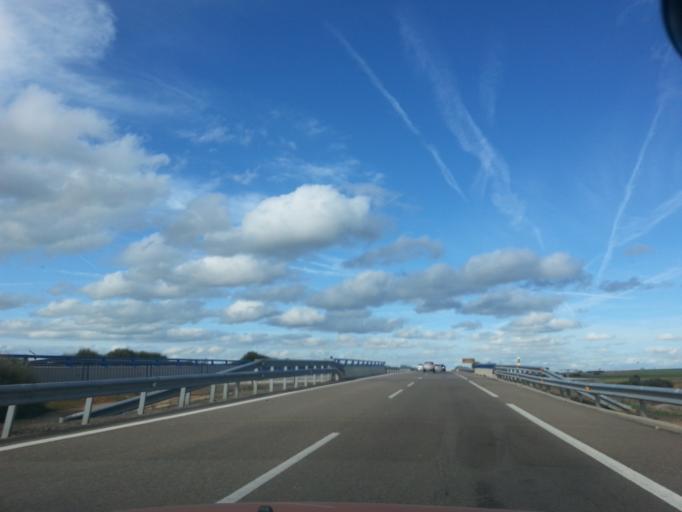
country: ES
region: Castille and Leon
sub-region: Provincia de Salamanca
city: Doninos de Salamanca
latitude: 40.9409
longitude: -5.7719
